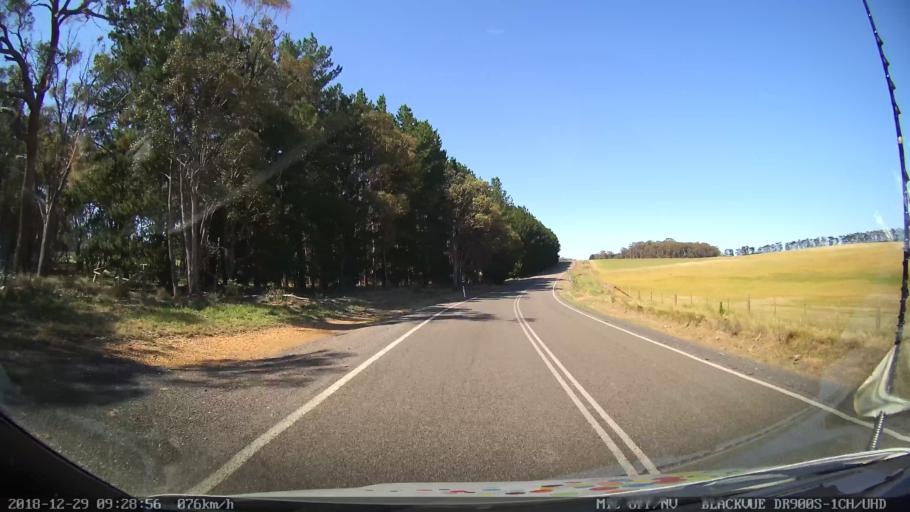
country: AU
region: New South Wales
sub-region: Upper Lachlan Shire
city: Crookwell
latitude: -34.5842
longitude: 149.3789
